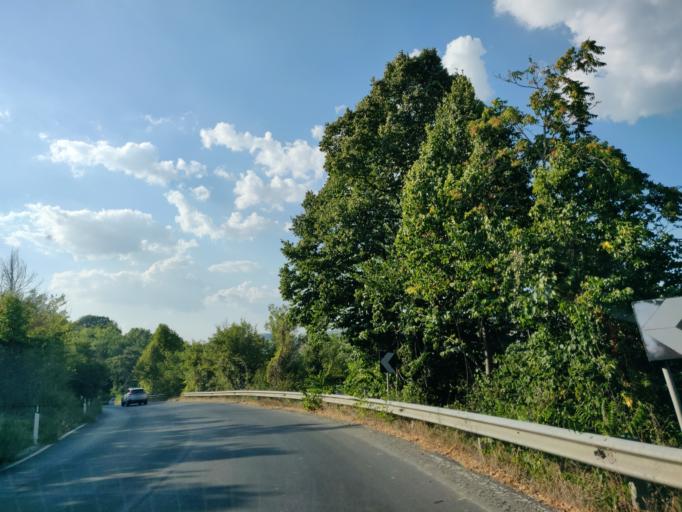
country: IT
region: Latium
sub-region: Provincia di Viterbo
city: Acquapendente
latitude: 42.7576
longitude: 11.8656
